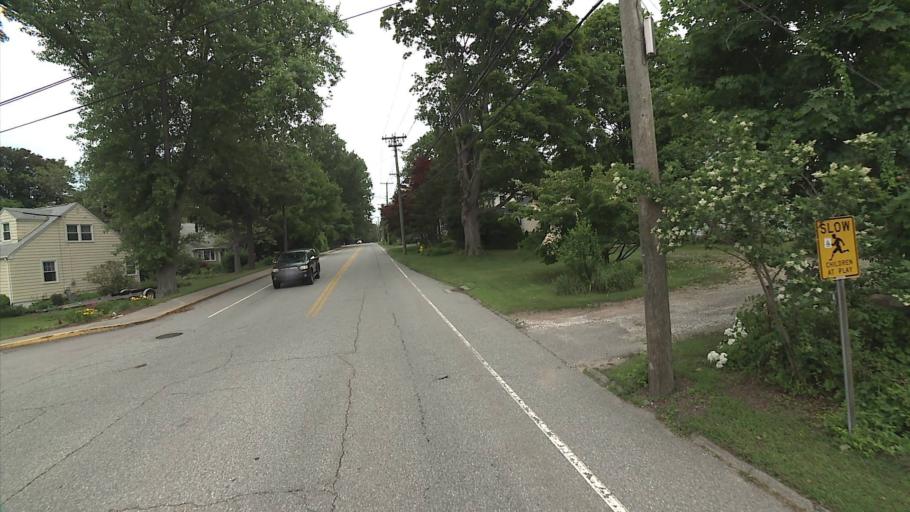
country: US
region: Connecticut
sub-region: New London County
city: Groton
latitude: 41.3273
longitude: -72.0733
